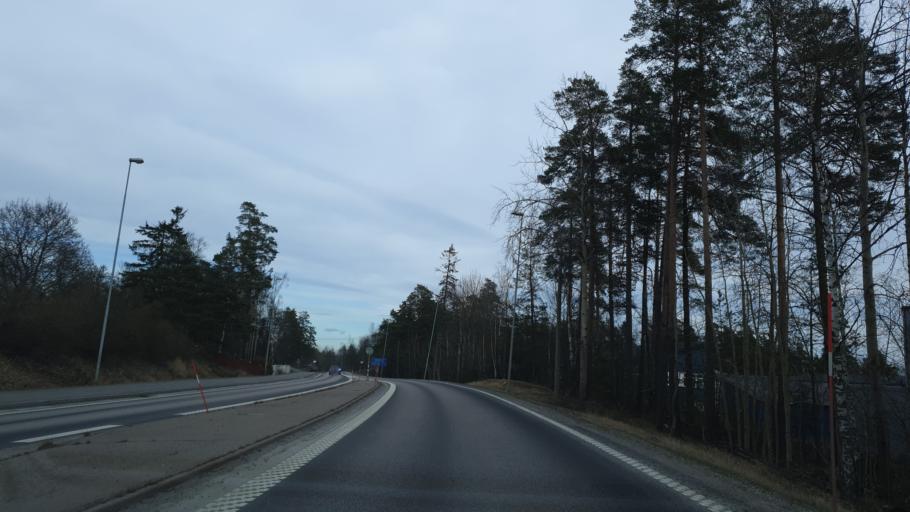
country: SE
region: Stockholm
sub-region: Vallentuna Kommun
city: Vallentuna
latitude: 59.5300
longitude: 18.1084
